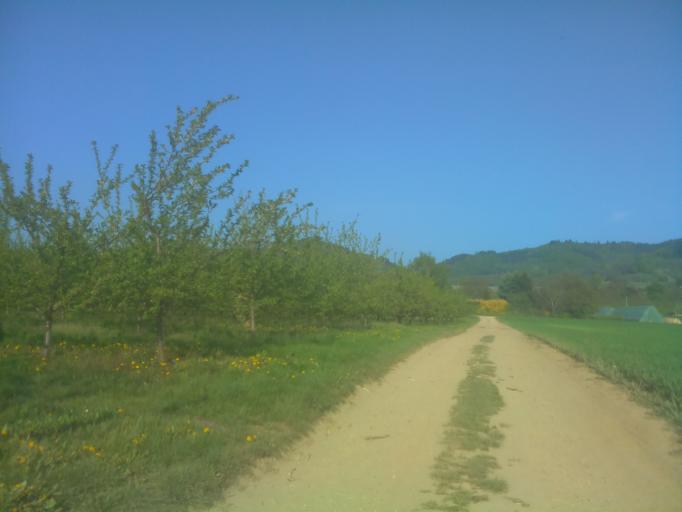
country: DE
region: Baden-Wuerttemberg
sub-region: Karlsruhe Region
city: Schriesheim
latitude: 49.5065
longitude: 8.6523
